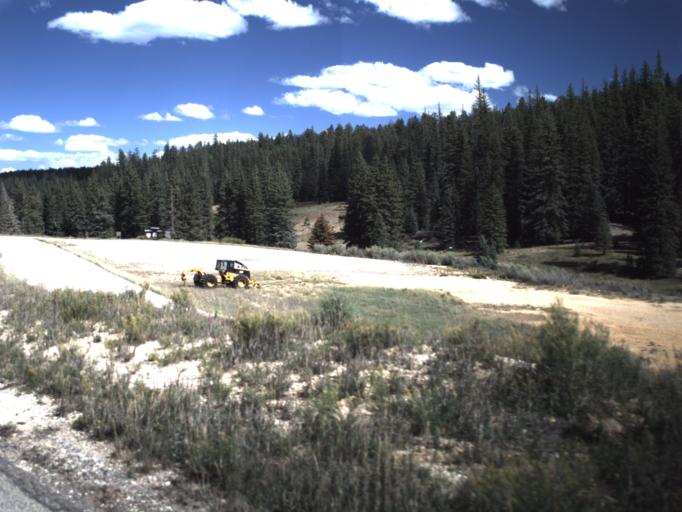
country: US
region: Utah
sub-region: Garfield County
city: Panguitch
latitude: 37.4980
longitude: -112.6031
